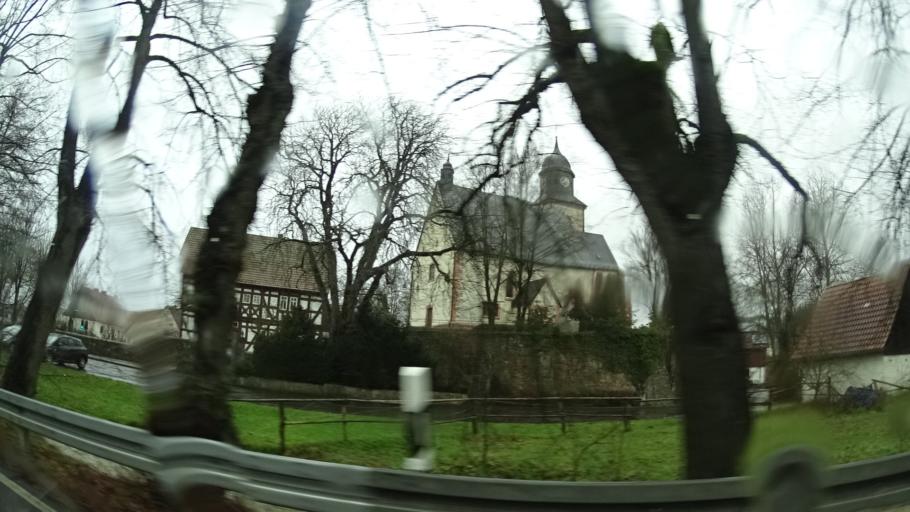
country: DE
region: Hesse
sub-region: Regierungsbezirk Kassel
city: Dipperz
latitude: 50.5655
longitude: 9.7613
